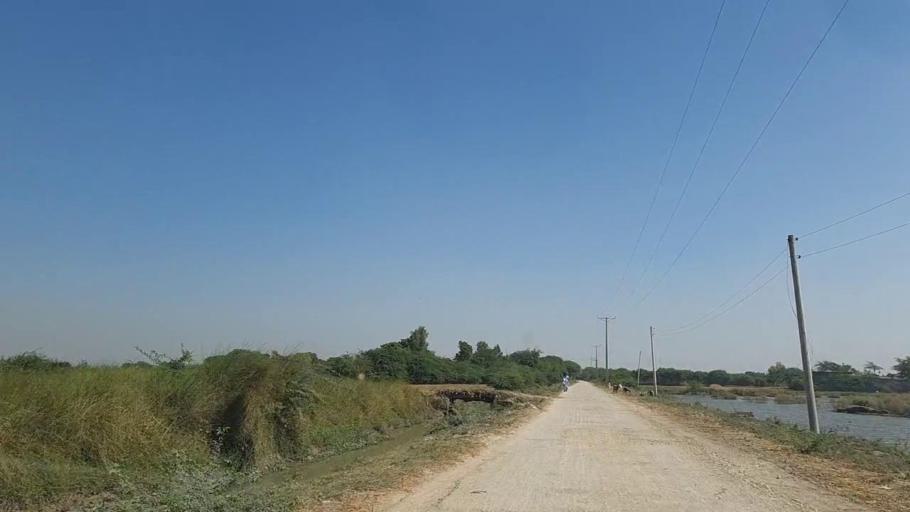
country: PK
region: Sindh
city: Daro Mehar
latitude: 24.7888
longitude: 68.1697
